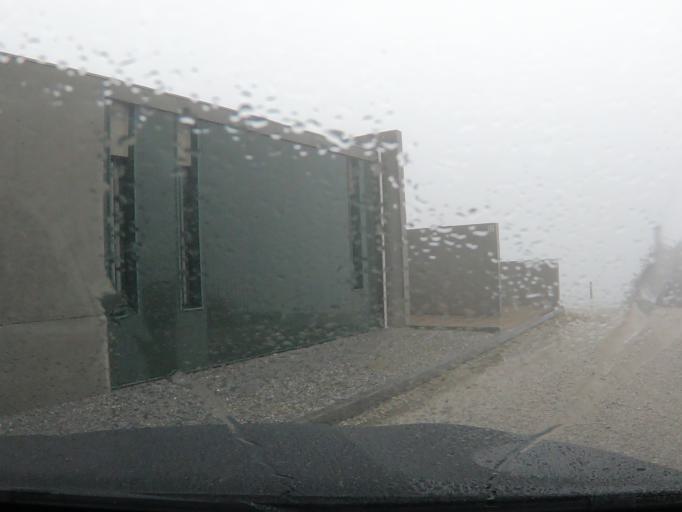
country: PT
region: Vila Real
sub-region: Mondim de Basto
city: Mondim de Basto
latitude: 41.3243
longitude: -7.8677
